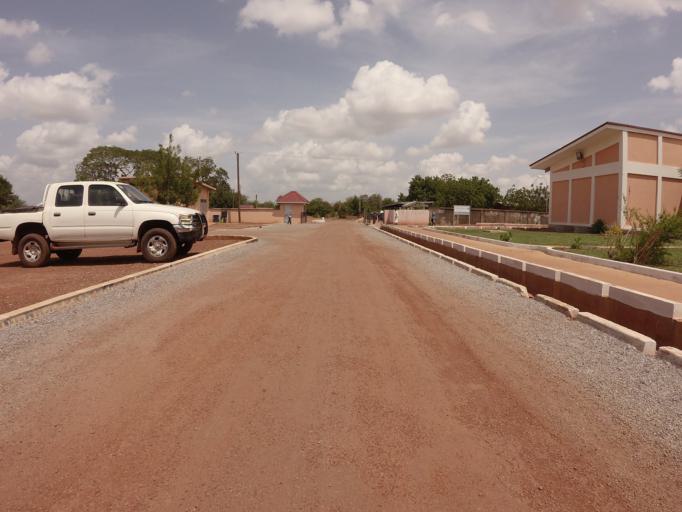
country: GH
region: Northern
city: Tamale
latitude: 9.3915
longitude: -0.8238
